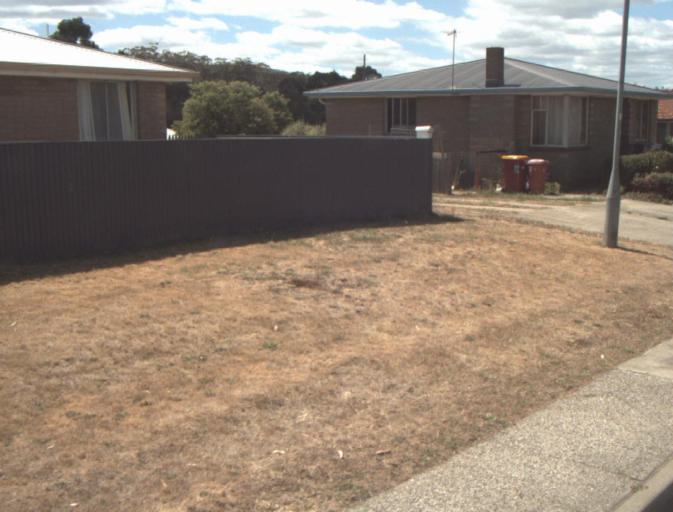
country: AU
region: Tasmania
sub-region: Launceston
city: Newstead
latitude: -41.4110
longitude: 147.1686
